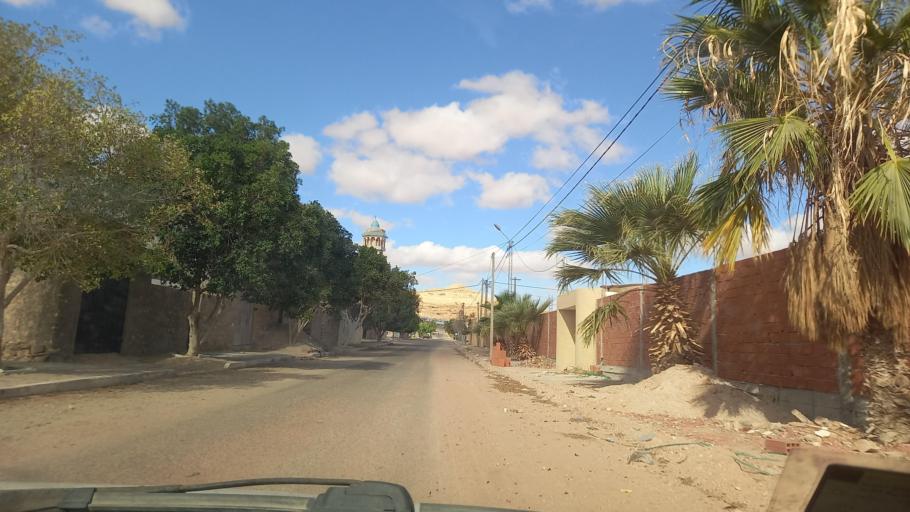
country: TN
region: Tataouine
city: Tataouine
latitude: 32.9803
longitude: 10.2689
